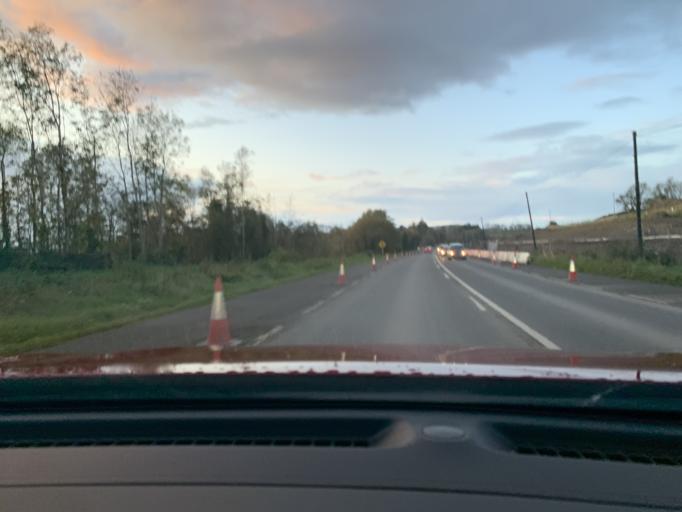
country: IE
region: Connaught
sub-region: Sligo
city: Collooney
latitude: 54.1630
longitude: -8.4820
